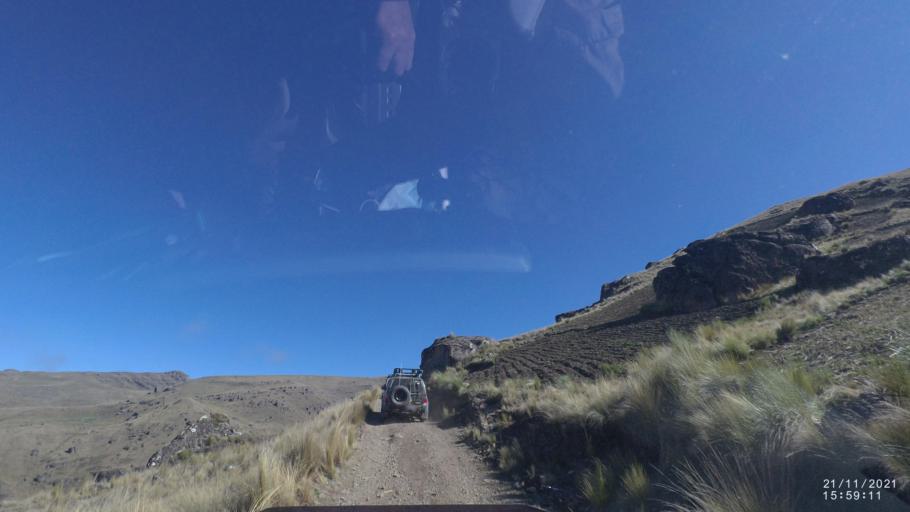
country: BO
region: Cochabamba
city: Cochabamba
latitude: -16.9792
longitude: -66.2635
